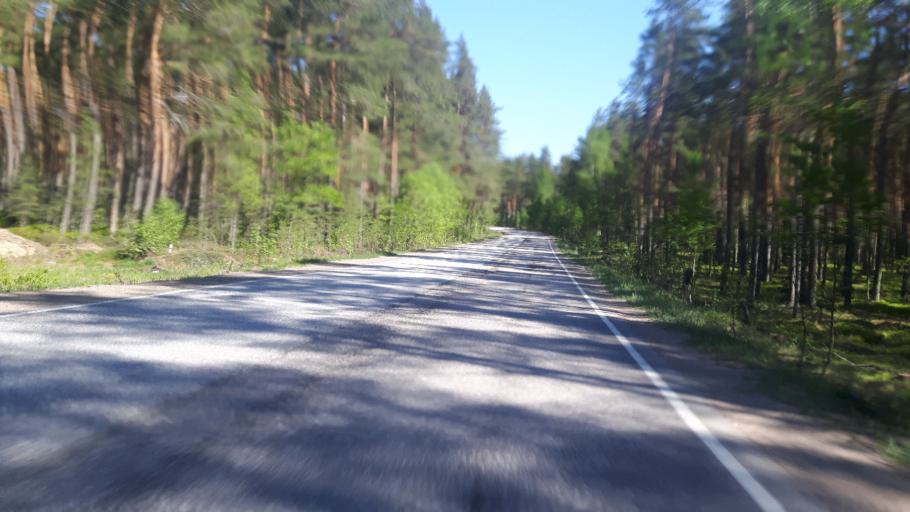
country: RU
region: Leningrad
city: Glebychevo
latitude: 60.2770
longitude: 28.9047
